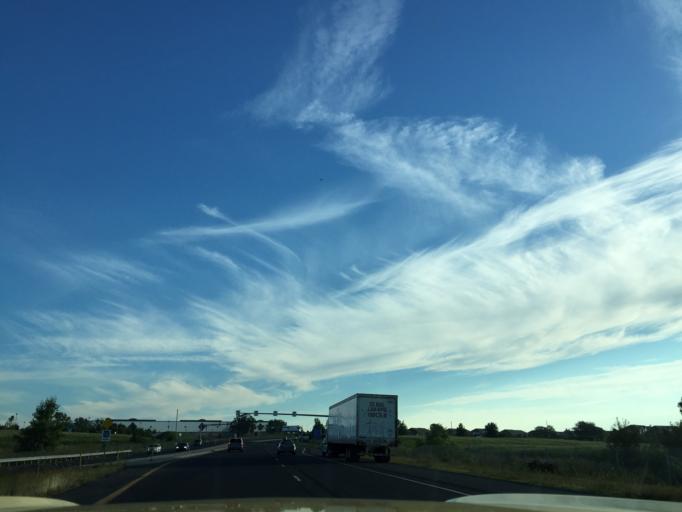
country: US
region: Pennsylvania
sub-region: Lehigh County
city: Trexlertown
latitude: 40.5488
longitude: -75.6211
